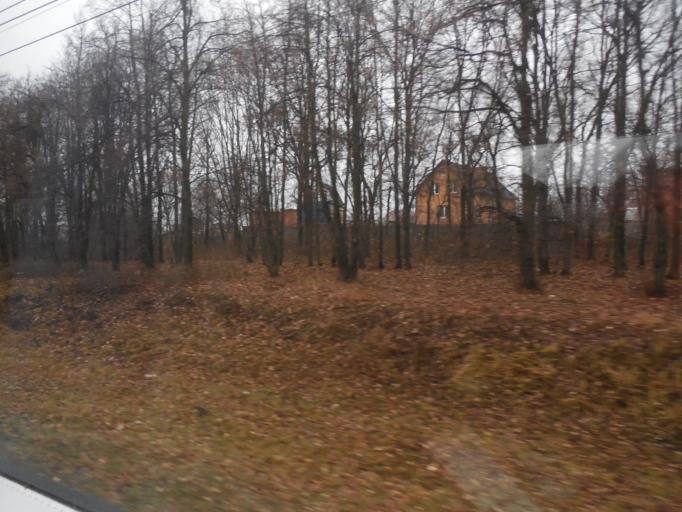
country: RU
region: Moscow
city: Zagor'ye
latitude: 55.5610
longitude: 37.6721
